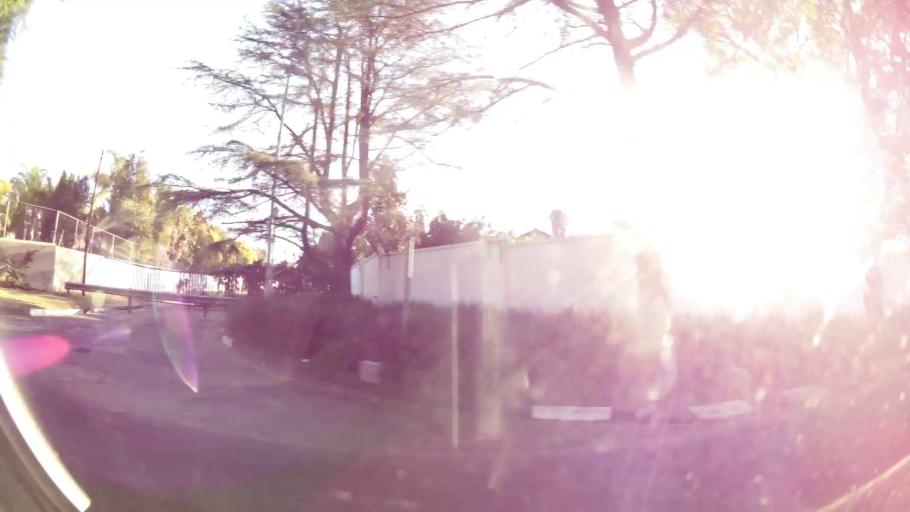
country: ZA
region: Gauteng
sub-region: City of Johannesburg Metropolitan Municipality
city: Modderfontein
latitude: -26.0851
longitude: 28.0693
